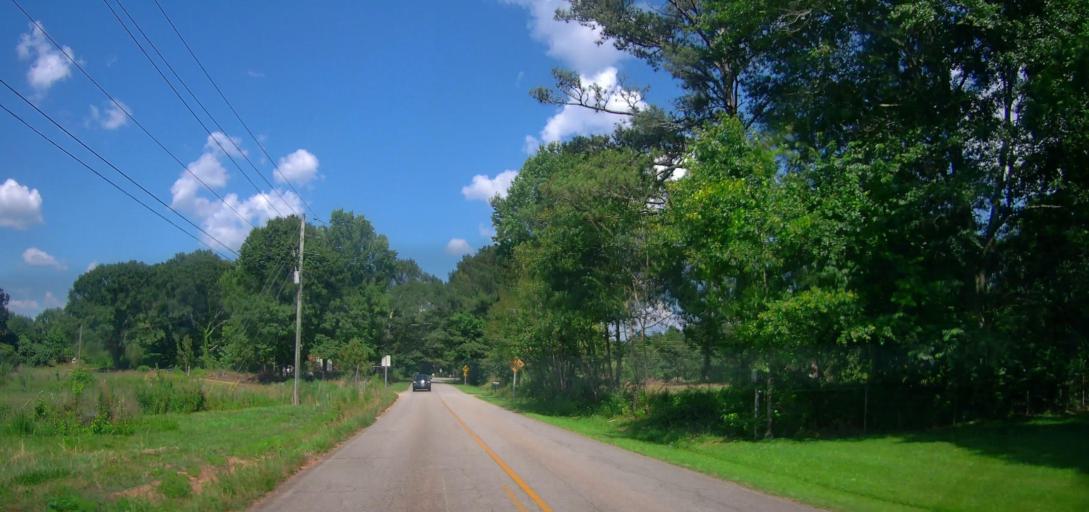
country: US
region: Georgia
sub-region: Spalding County
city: East Griffin
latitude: 33.2315
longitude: -84.1306
